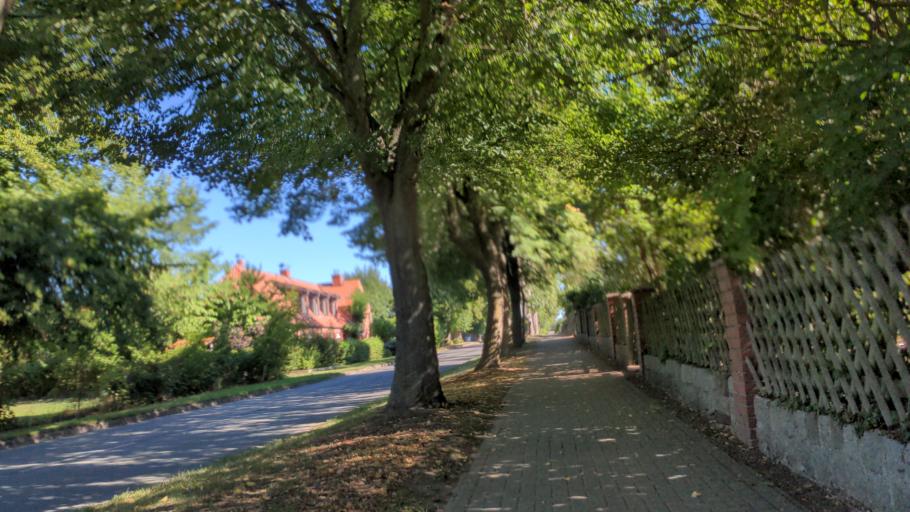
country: DE
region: Mecklenburg-Vorpommern
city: Gramkow
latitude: 53.9316
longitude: 11.3309
